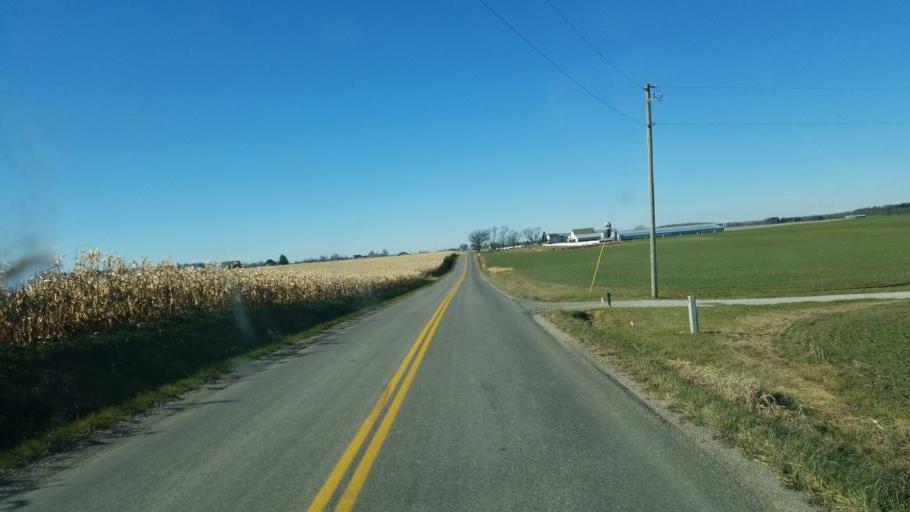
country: US
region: Ohio
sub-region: Ashland County
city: Ashland
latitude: 40.9532
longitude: -82.4108
